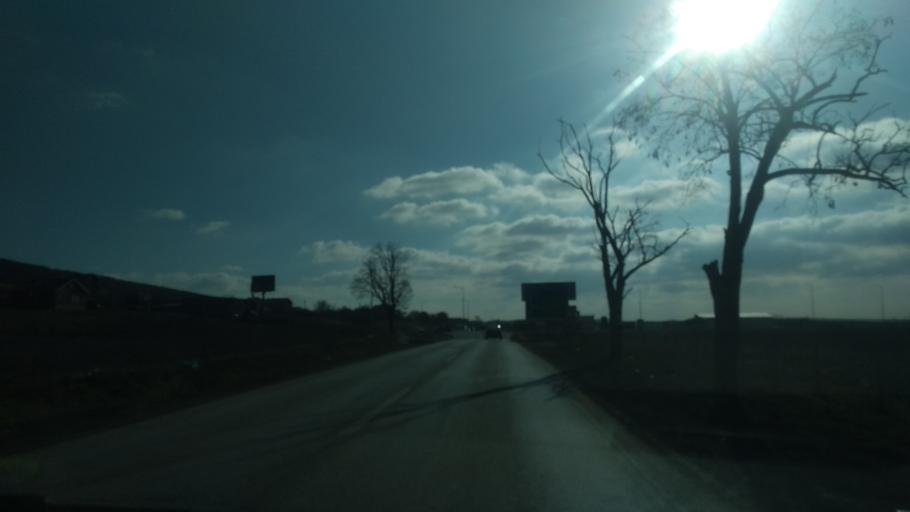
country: XK
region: Pristina
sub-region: Komuna e Prishtines
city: Pristina
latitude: 42.7341
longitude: 21.1420
